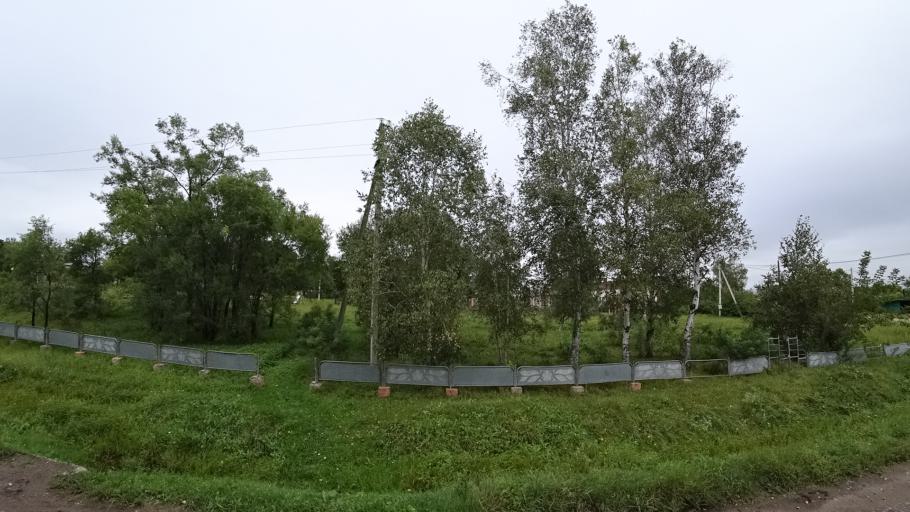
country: RU
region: Primorskiy
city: Monastyrishche
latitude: 44.0803
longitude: 132.5811
